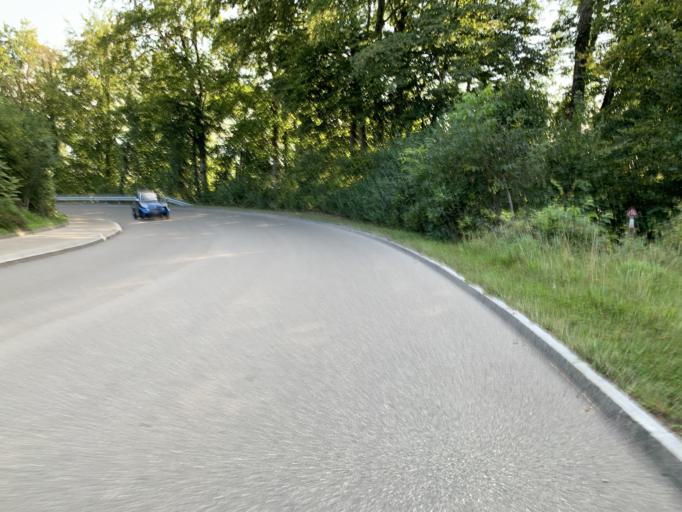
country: CH
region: Zurich
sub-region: Bezirk Hinwil
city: Hinwil
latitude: 47.3067
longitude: 8.8425
